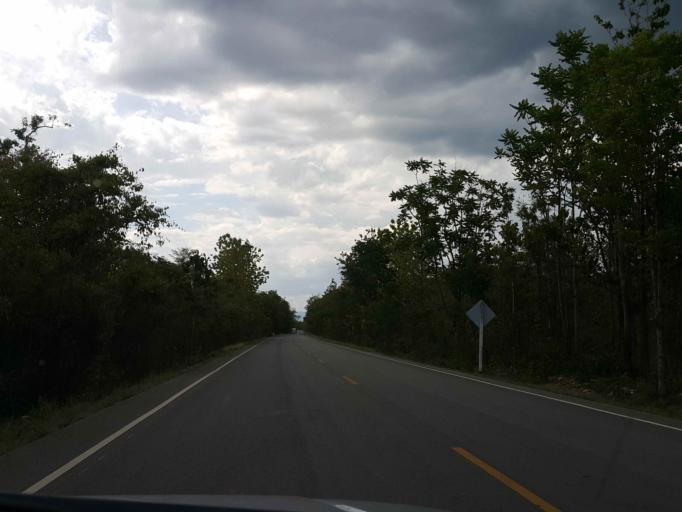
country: TH
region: Sukhothai
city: Thung Saliam
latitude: 17.3672
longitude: 99.4076
